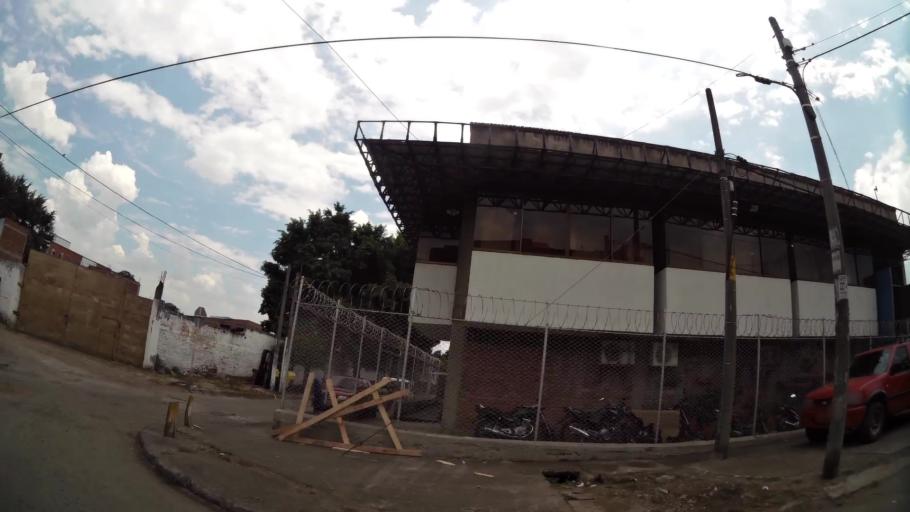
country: CO
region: Valle del Cauca
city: Cali
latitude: 3.4693
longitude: -76.5074
